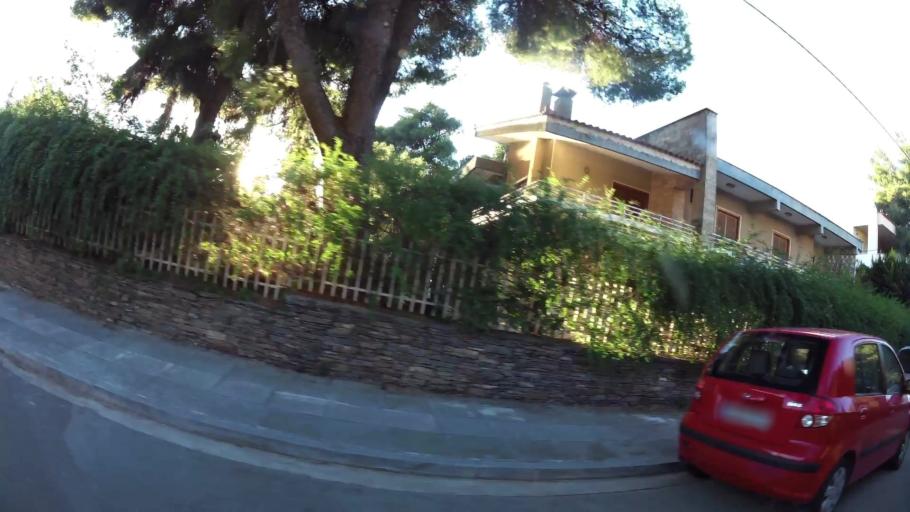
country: GR
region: Attica
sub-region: Nomarchia Athinas
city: Nea Erythraia
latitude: 38.0864
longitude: 23.8258
